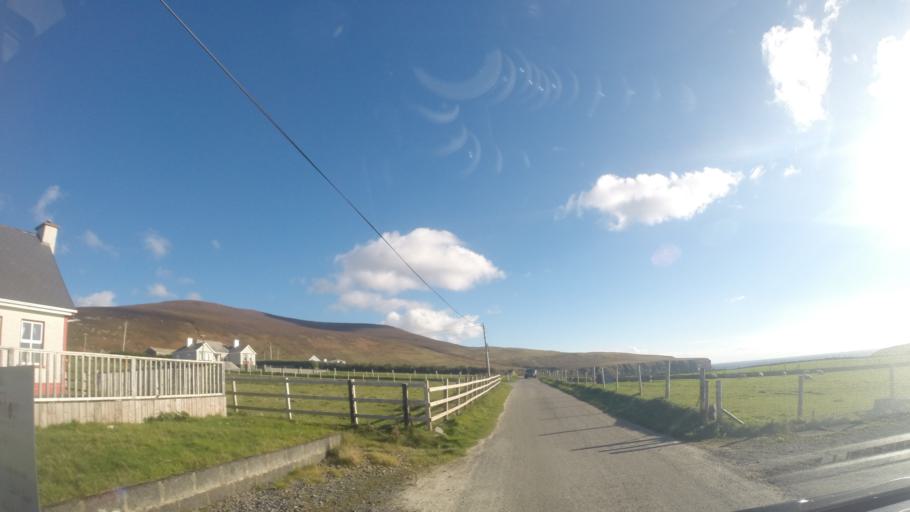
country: IE
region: Ulster
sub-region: County Donegal
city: Killybegs
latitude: 54.6662
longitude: -8.7796
